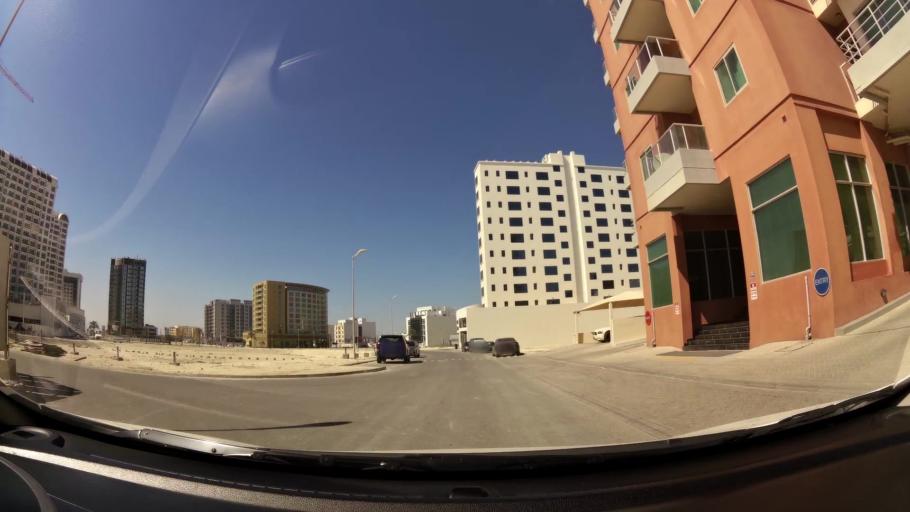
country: BH
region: Muharraq
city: Al Hadd
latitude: 26.2904
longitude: 50.6674
